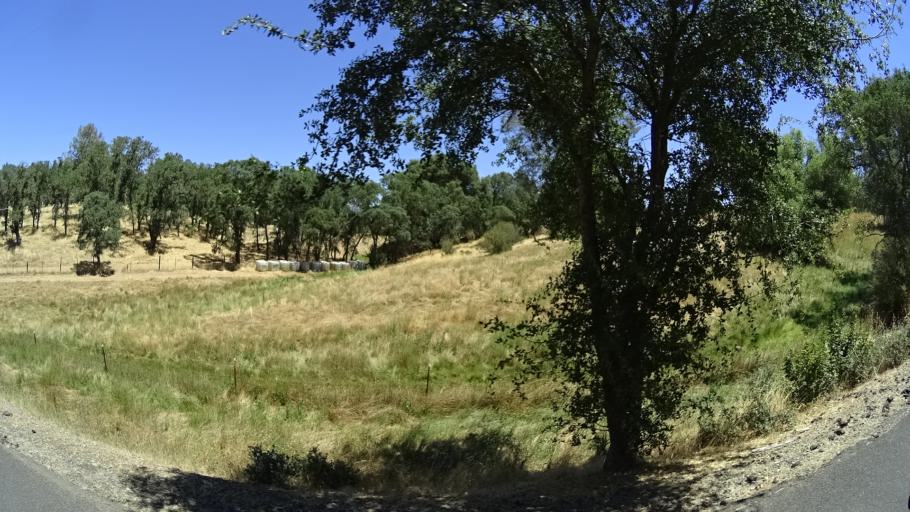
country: US
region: California
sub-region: Calaveras County
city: Copperopolis
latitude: 37.9808
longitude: -120.6799
